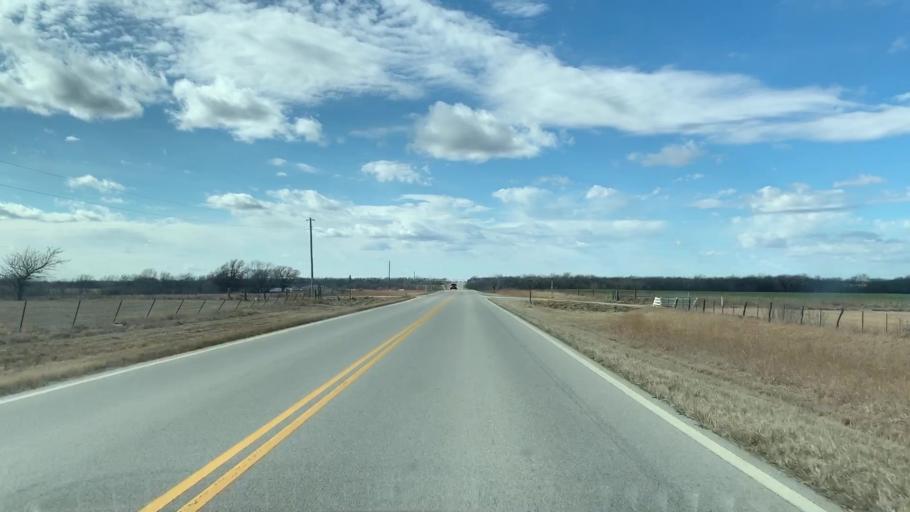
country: US
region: Kansas
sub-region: Neosho County
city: Chanute
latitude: 37.5288
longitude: -95.4513
